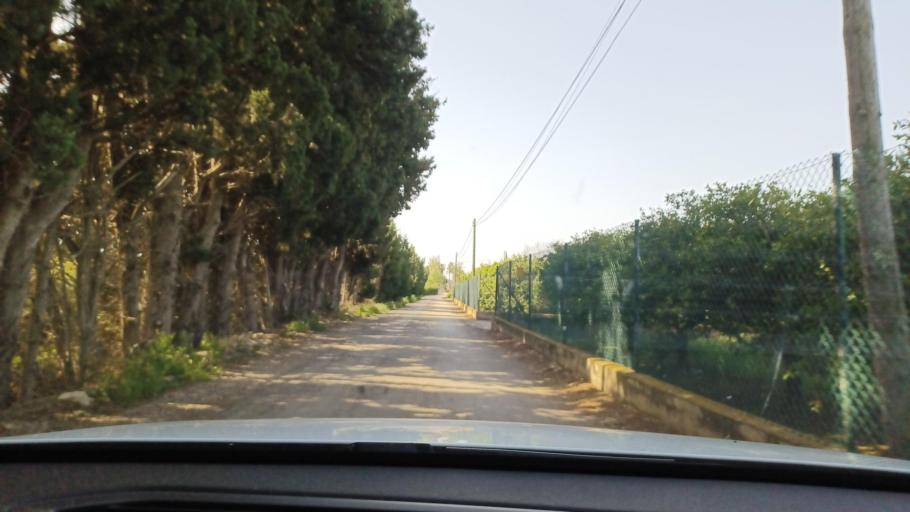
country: ES
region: Catalonia
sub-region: Provincia de Tarragona
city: Tortosa
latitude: 40.7952
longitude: 0.5160
